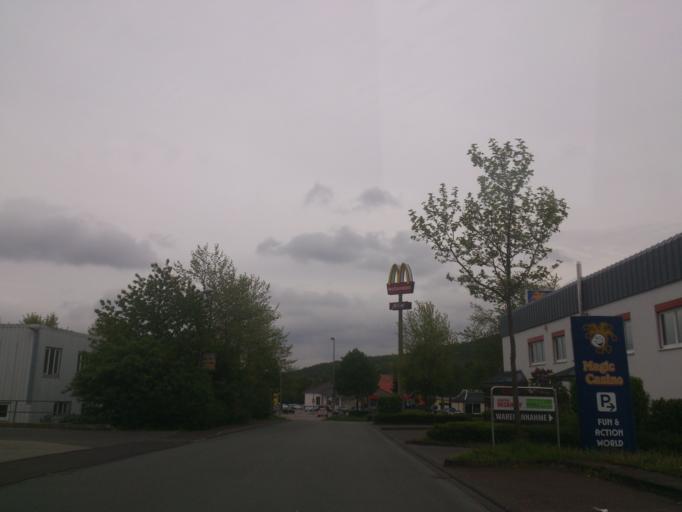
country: DE
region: North Rhine-Westphalia
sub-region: Regierungsbezirk Detmold
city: Bad Driburg
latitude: 51.7204
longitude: 9.0147
